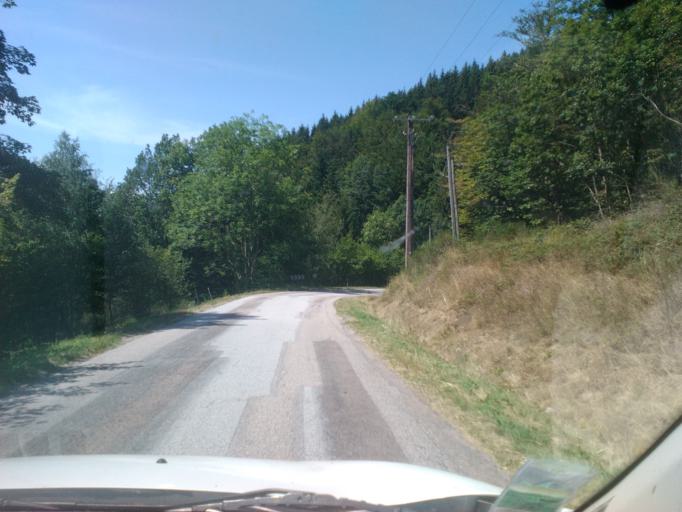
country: FR
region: Lorraine
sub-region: Departement des Vosges
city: La Bresse
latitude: 48.0375
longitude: 6.8072
